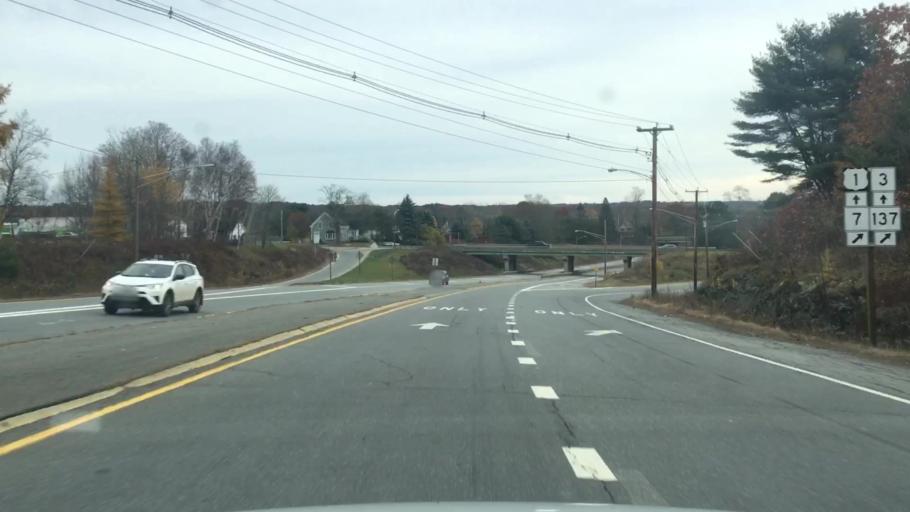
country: US
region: Maine
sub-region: Waldo County
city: Belfast
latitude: 44.4300
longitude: -69.0197
